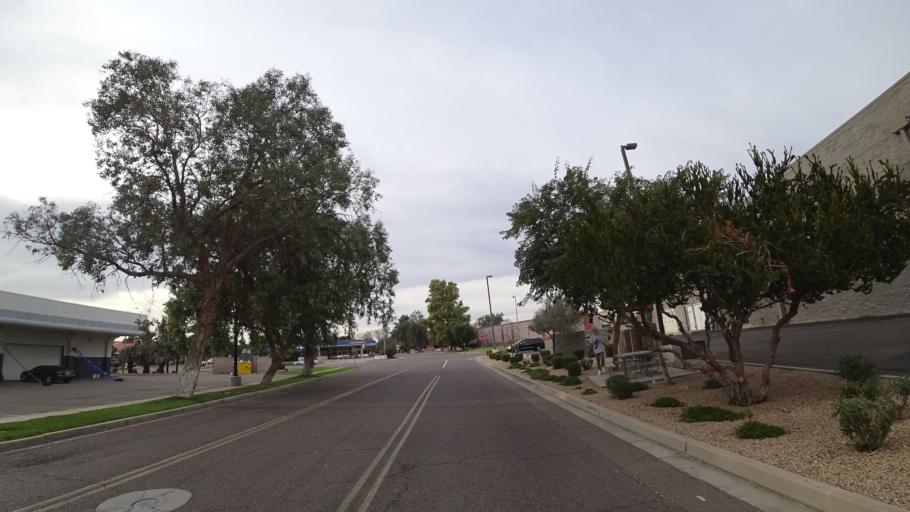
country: US
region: Arizona
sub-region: Maricopa County
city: Glendale
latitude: 33.5784
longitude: -112.1236
